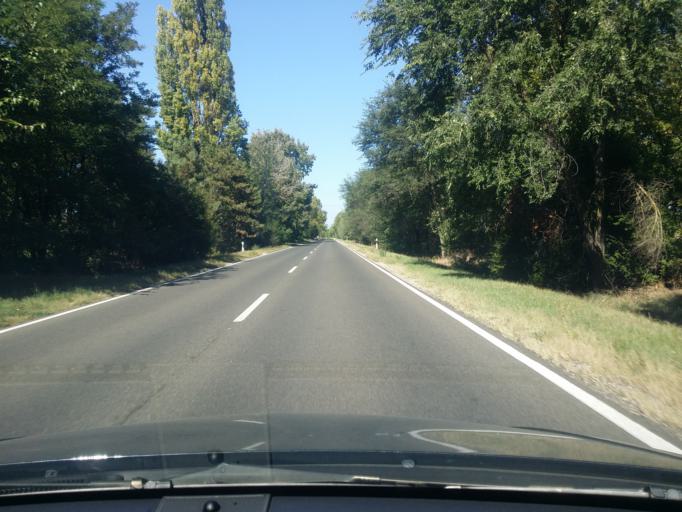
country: HU
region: Bacs-Kiskun
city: Palmonostora
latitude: 46.6271
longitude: 19.8968
